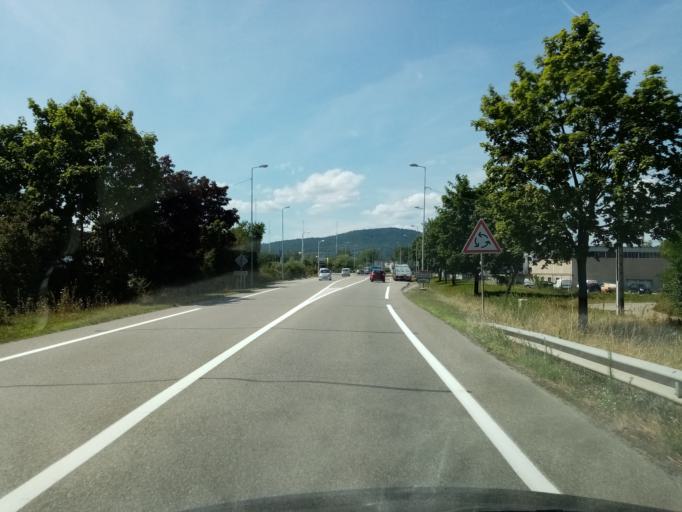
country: FR
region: Alsace
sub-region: Departement du Bas-Rhin
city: Selestat
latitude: 48.2487
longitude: 7.4392
